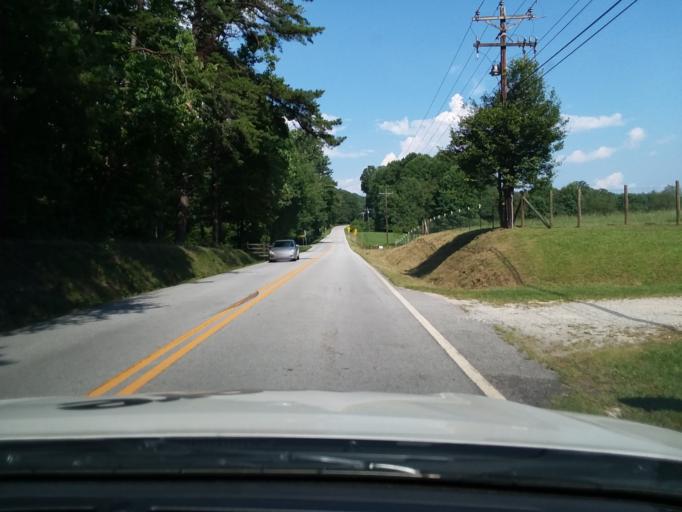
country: US
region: Georgia
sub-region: Rabun County
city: Clayton
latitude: 34.8580
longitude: -83.4620
